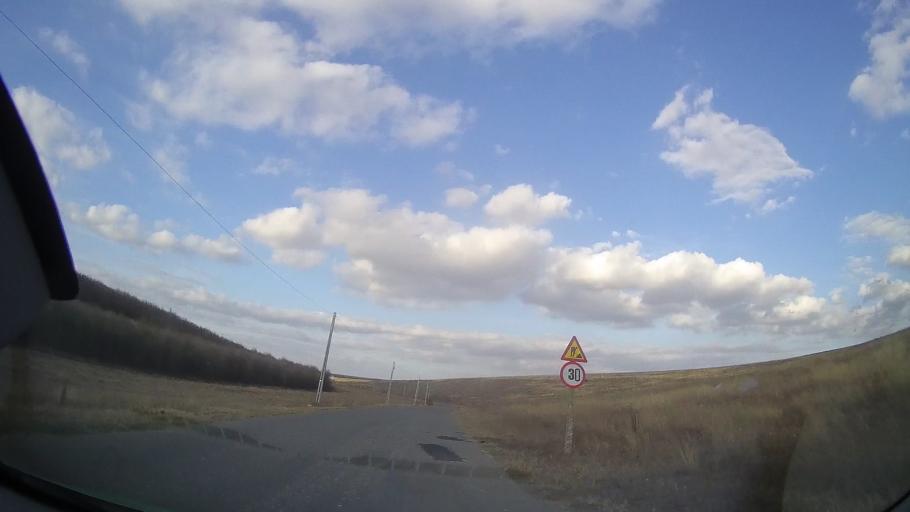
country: RO
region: Constanta
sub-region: Comuna Cerchezu
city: Cerchezu
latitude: 43.8331
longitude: 28.0966
